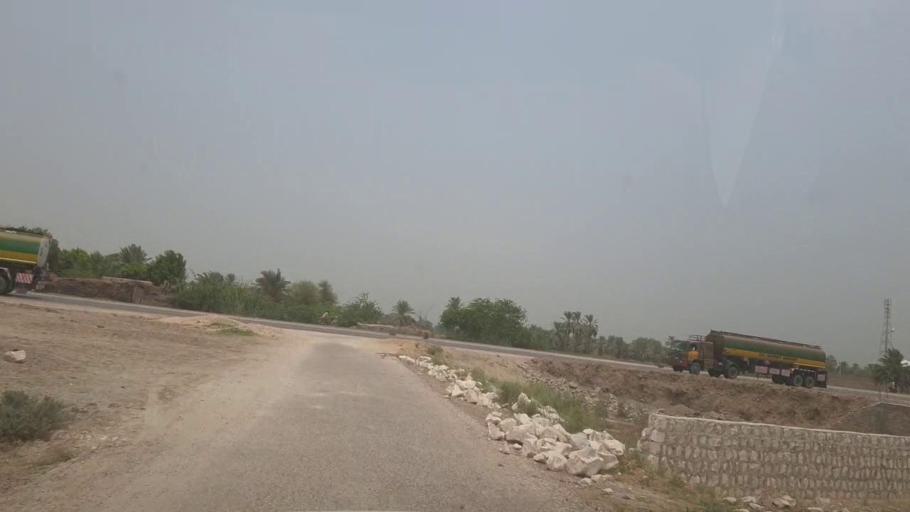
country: PK
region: Sindh
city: Kot Diji
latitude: 27.4460
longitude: 68.6399
